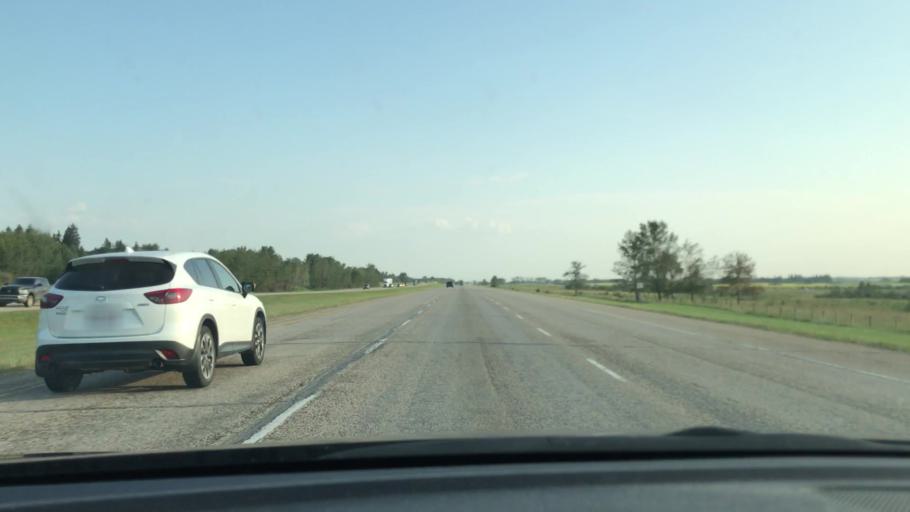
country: CA
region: Alberta
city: Lacombe
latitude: 52.5414
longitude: -113.6691
